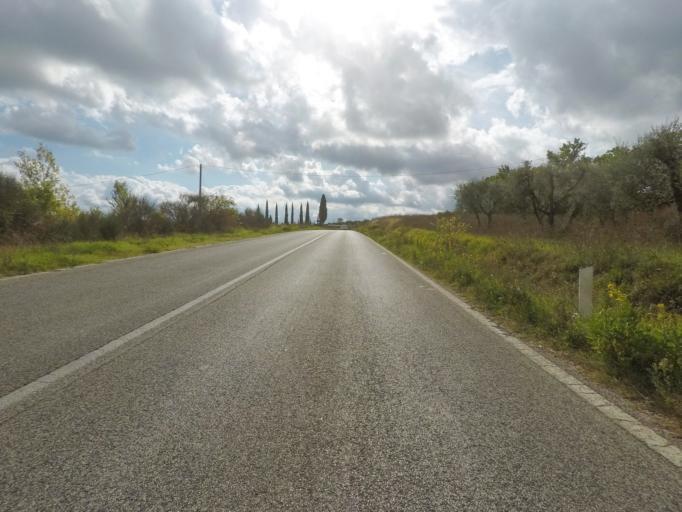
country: IT
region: Tuscany
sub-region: Provincia di Siena
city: Torrita di Siena
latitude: 43.1529
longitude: 11.7773
